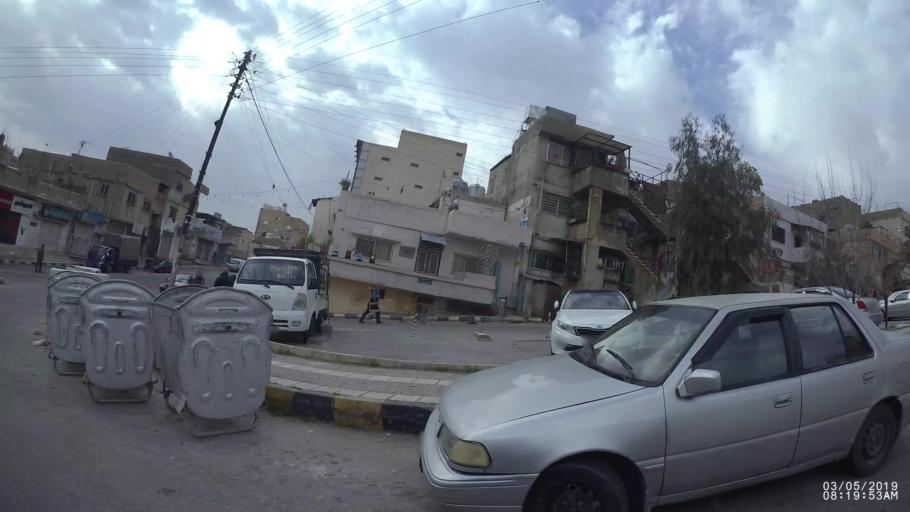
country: JO
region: Amman
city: Amman
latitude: 31.9733
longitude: 35.9227
